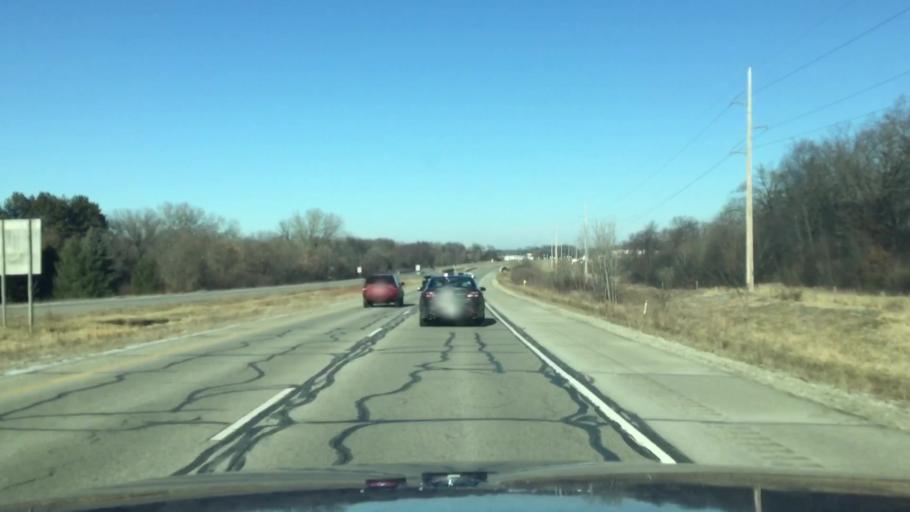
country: US
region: Wisconsin
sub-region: Racine County
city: Rochester
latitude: 42.7440
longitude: -88.2142
